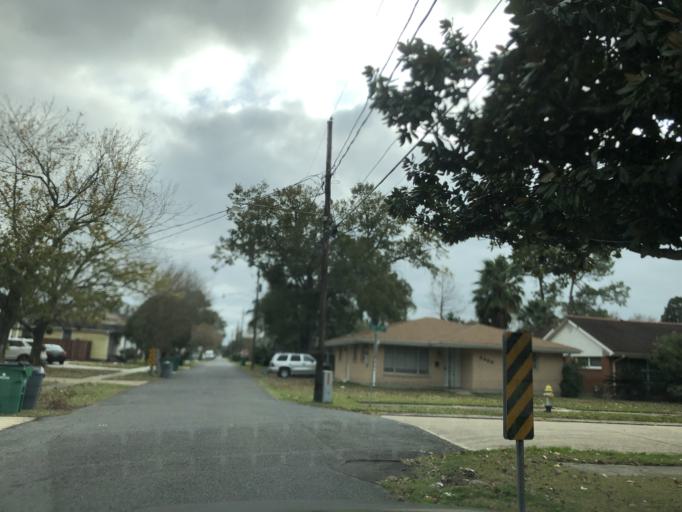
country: US
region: Louisiana
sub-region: Jefferson Parish
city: Metairie
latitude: 29.9871
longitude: -90.1589
